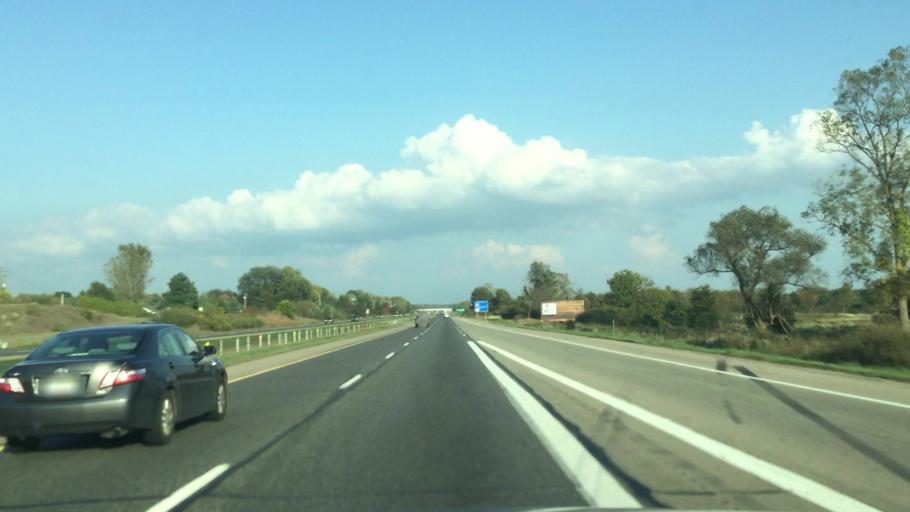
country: US
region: Michigan
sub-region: Washtenaw County
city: Chelsea
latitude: 42.2964
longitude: -83.9960
